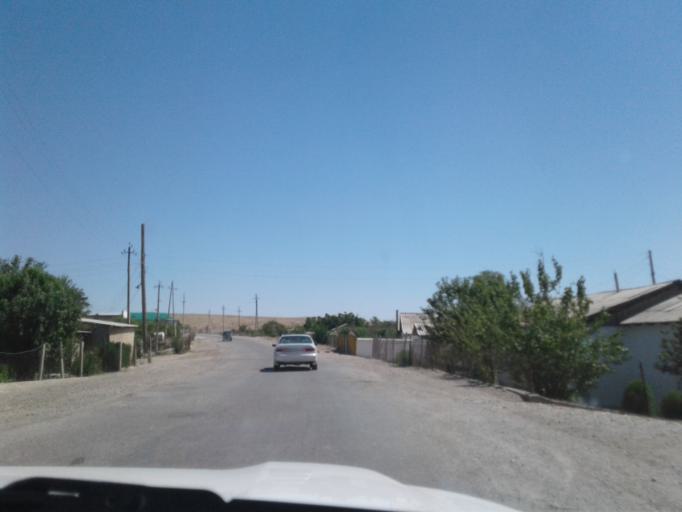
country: AF
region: Badghis
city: Bala Murghab
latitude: 35.9562
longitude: 62.9053
